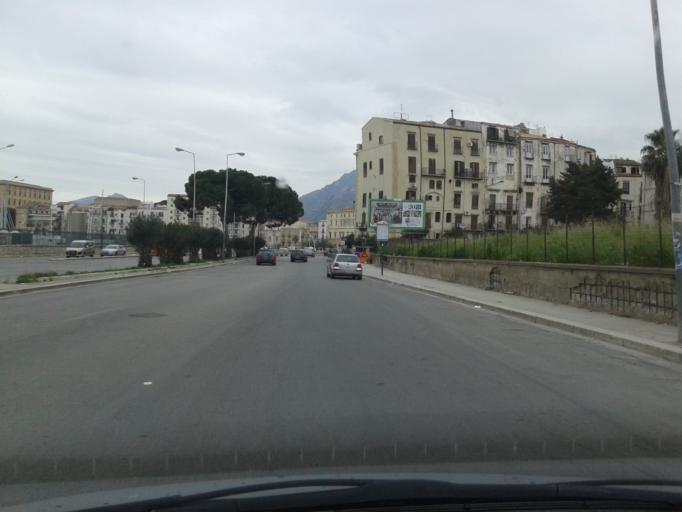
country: IT
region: Sicily
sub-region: Palermo
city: Palermo
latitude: 38.1213
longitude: 13.3659
